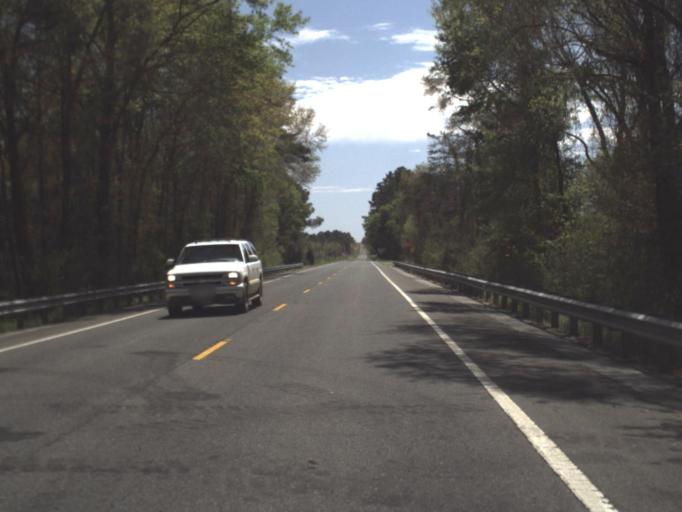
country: US
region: Alabama
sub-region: Geneva County
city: Samson
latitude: 30.9924
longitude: -85.9973
